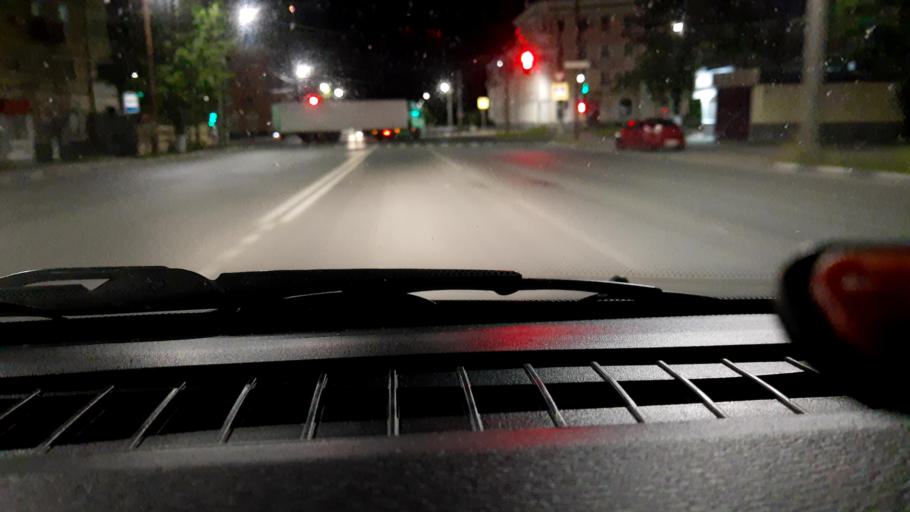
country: RU
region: Nizjnij Novgorod
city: Dzerzhinsk
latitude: 56.2402
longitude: 43.4832
